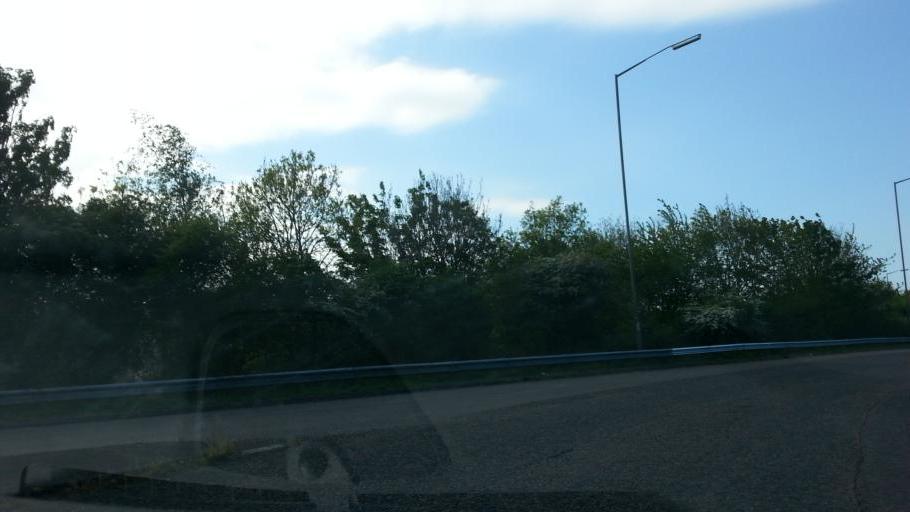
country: GB
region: England
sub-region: Peterborough
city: Peterborough
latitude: 52.5638
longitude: -0.2855
